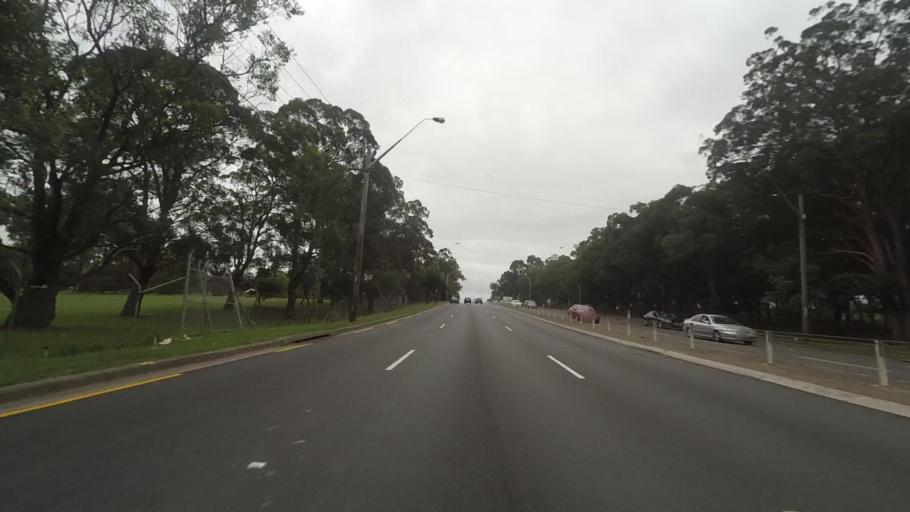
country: AU
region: New South Wales
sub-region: Auburn
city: Berala
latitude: -33.8756
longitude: 151.0415
